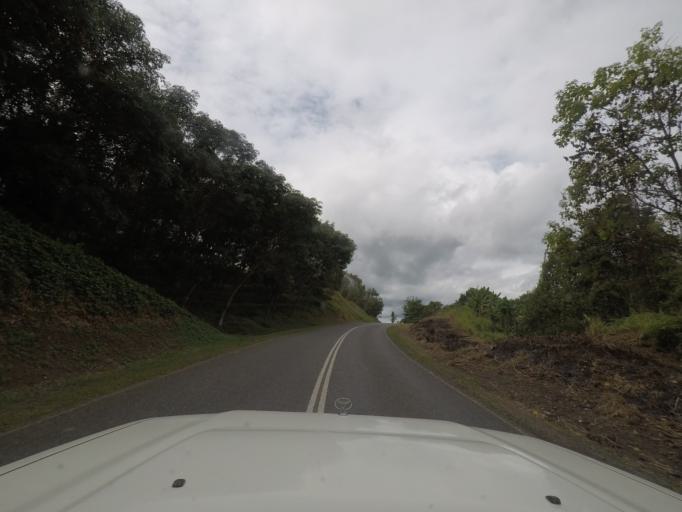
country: PG
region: National Capital
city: Port Moresby
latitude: -8.9875
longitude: 146.9671
